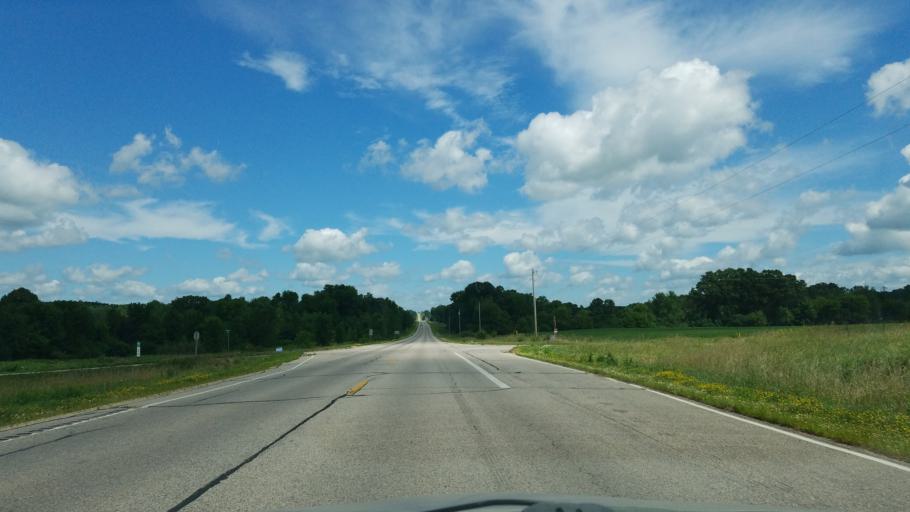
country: US
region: Wisconsin
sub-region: Saint Croix County
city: Glenwood City
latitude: 44.9875
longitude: -92.1965
